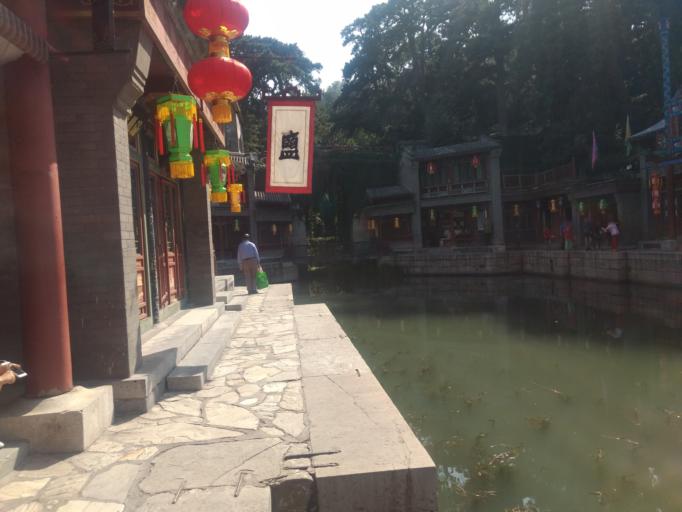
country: CN
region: Beijing
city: Haidian
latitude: 40.0006
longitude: 116.2692
